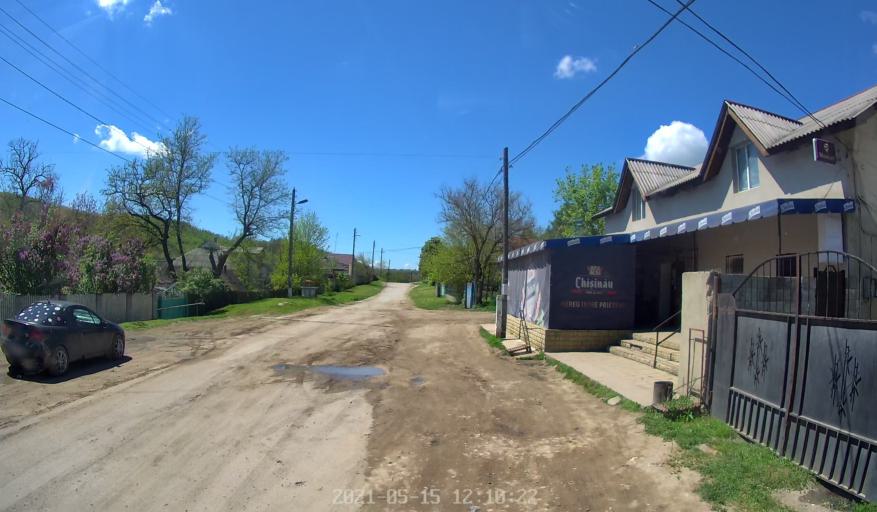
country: MD
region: Hincesti
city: Hincesti
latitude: 46.7964
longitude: 28.5402
